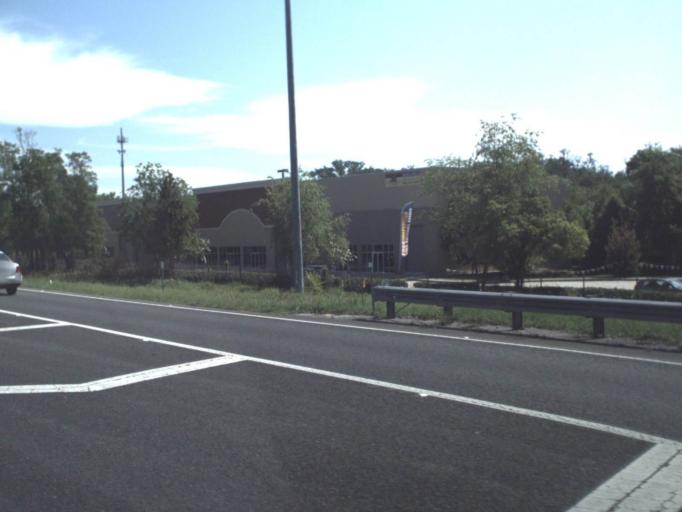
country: US
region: Florida
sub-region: Clay County
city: Bellair-Meadowbrook Terrace
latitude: 30.2446
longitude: -81.7627
